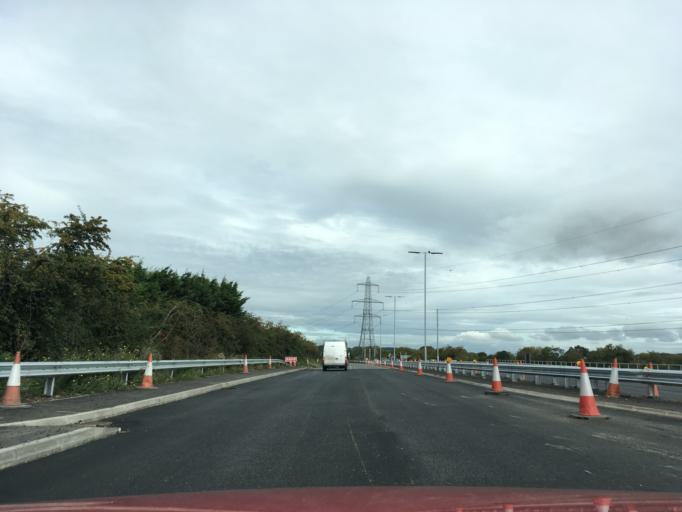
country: GB
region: England
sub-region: Gloucestershire
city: Barnwood
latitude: 51.8792
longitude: -2.2014
